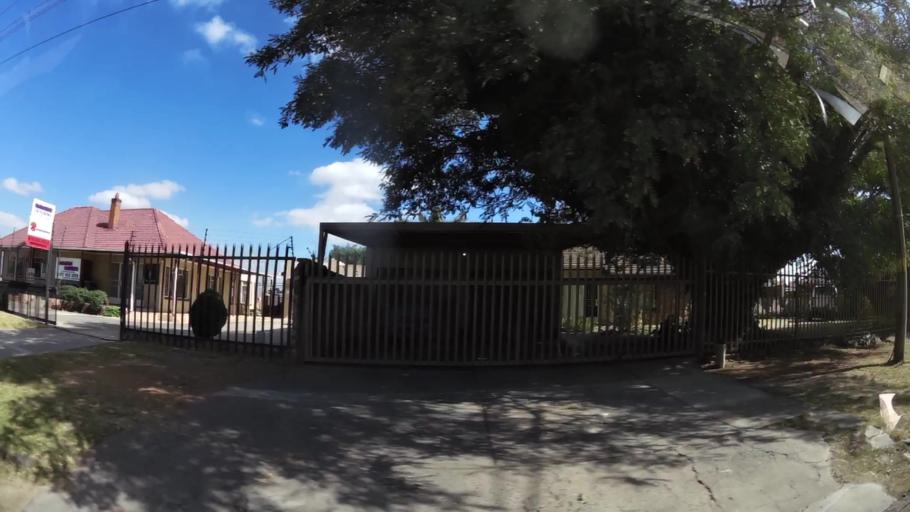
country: ZA
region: Gauteng
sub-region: West Rand District Municipality
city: Krugersdorp
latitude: -26.1224
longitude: 27.8233
